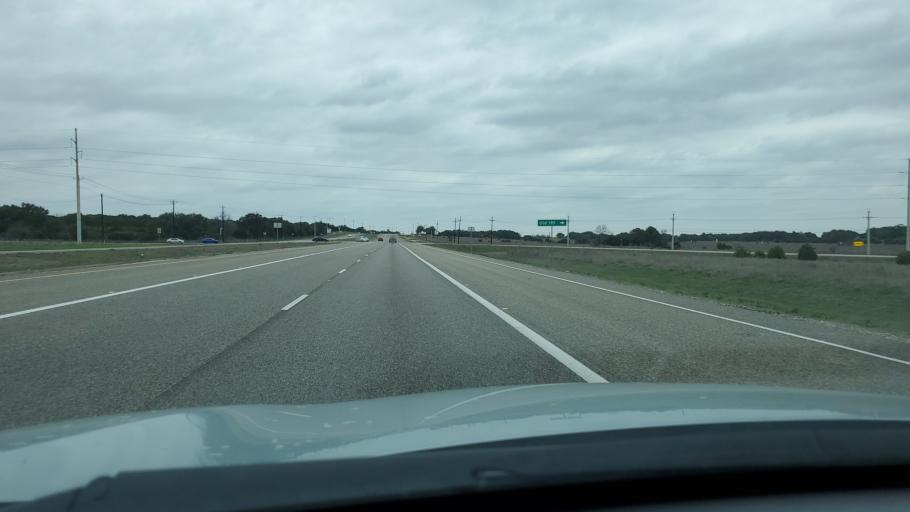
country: US
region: Texas
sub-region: Williamson County
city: Florence
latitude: 30.7871
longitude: -97.7641
